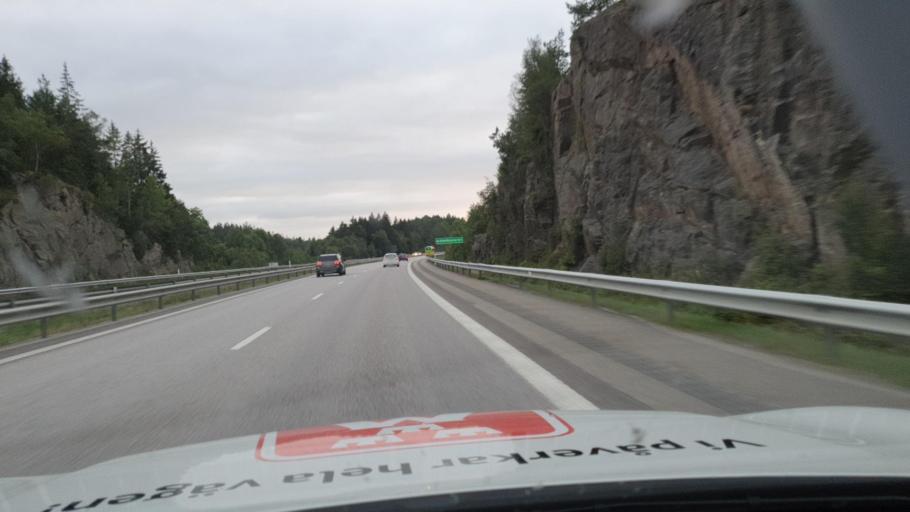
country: SE
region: Vaestra Goetaland
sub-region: Harryda Kommun
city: Landvetter
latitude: 57.6839
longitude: 12.2596
